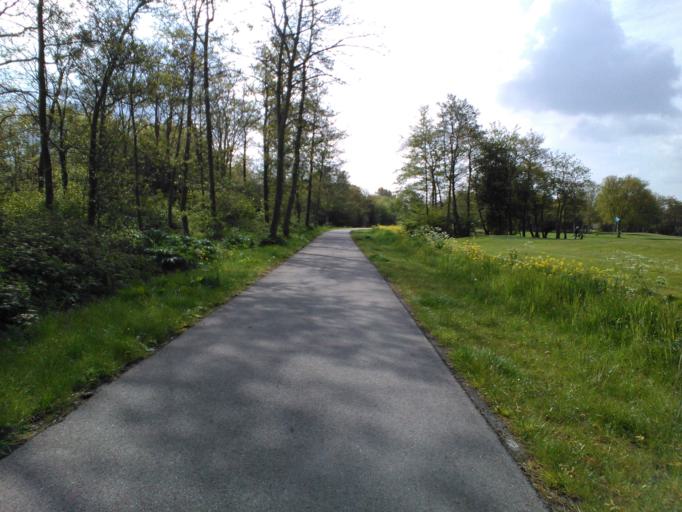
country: NL
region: South Holland
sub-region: Gemeente Vlaardingen
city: Vlaardingen
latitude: 51.9107
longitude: 4.3082
